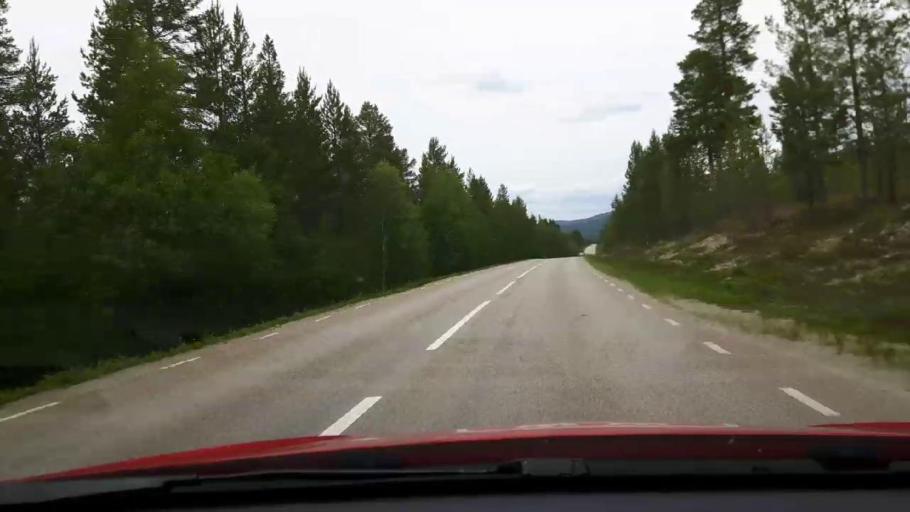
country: SE
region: Jaemtland
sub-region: Harjedalens Kommun
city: Sveg
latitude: 62.2462
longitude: 13.8436
